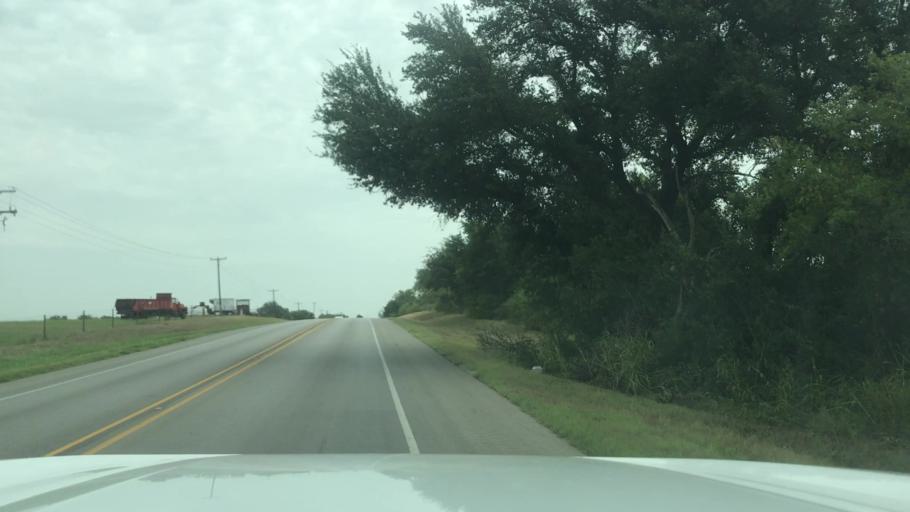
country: US
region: Texas
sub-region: Erath County
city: Dublin
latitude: 32.0933
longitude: -98.4146
